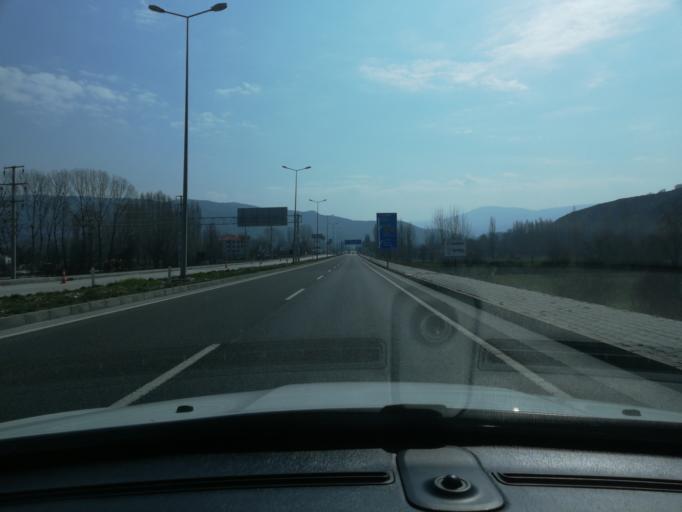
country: TR
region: Cankiri
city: Ilgaz
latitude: 40.9070
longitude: 33.6412
